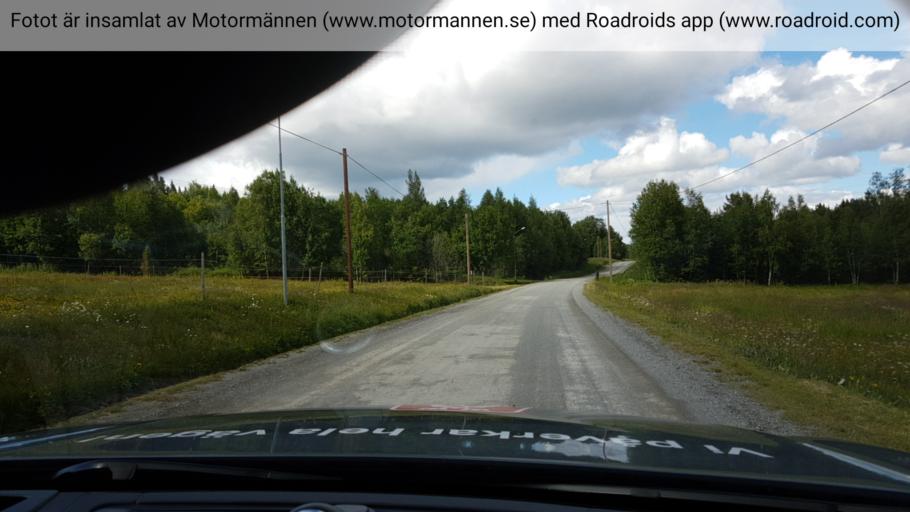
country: SE
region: Jaemtland
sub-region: Bergs Kommun
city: Hoverberg
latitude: 62.8876
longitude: 14.3078
